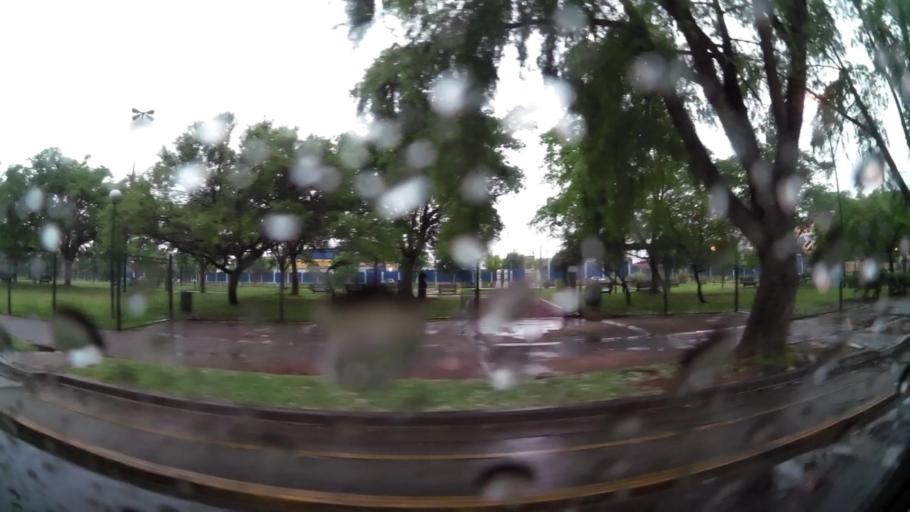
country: AR
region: Buenos Aires F.D.
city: Buenos Aires
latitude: -34.6334
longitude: -58.3675
